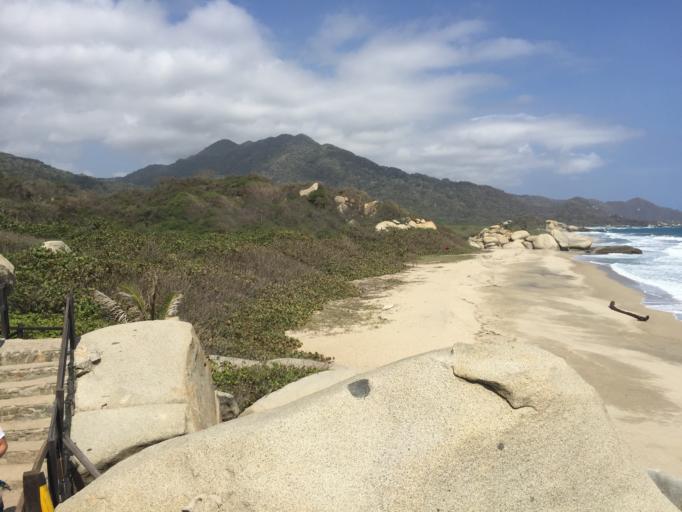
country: CO
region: Magdalena
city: Santa Marta
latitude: 11.3118
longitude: -73.9389
